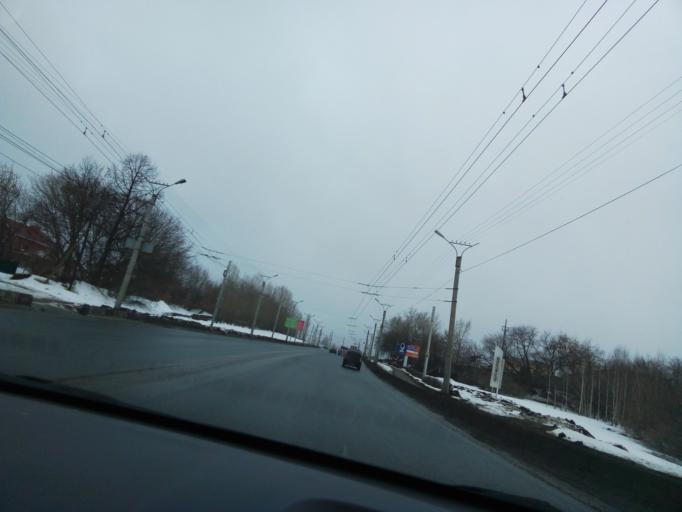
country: RU
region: Chuvashia
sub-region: Cheboksarskiy Rayon
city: Cheboksary
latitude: 56.1262
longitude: 47.2169
